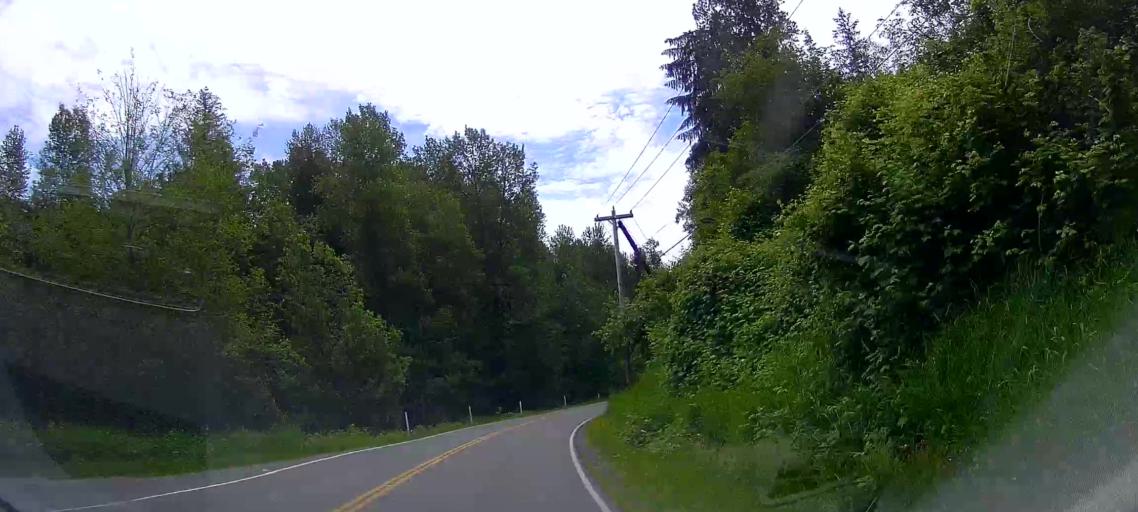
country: US
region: Washington
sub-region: Snohomish County
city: Bryant
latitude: 48.2388
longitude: -122.2195
